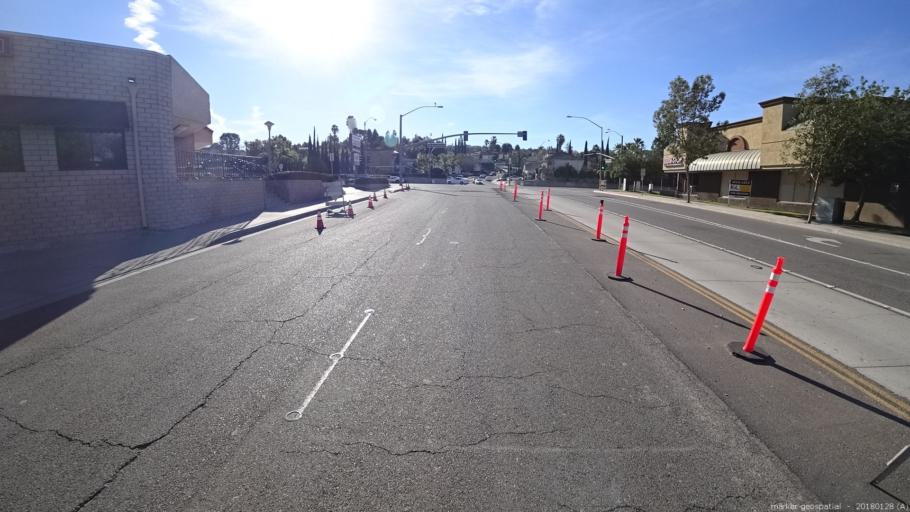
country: US
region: California
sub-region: Los Angeles County
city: Walnut
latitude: 33.9976
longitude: -117.8545
